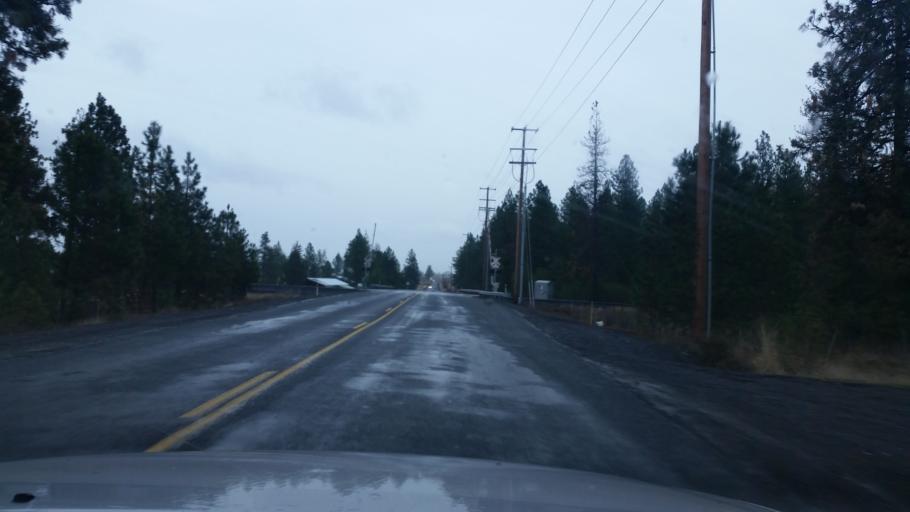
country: US
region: Washington
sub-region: Spokane County
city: Airway Heights
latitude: 47.6719
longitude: -117.5866
